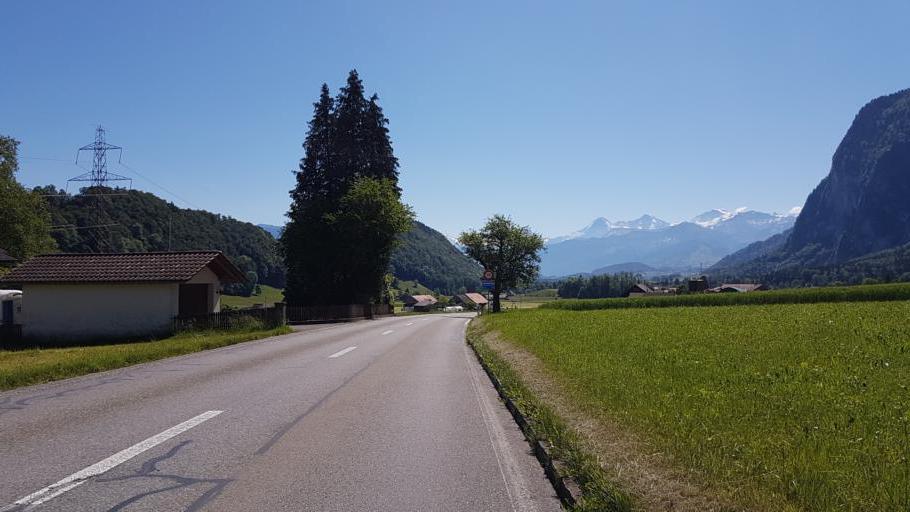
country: CH
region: Bern
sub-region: Thun District
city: Thierachern
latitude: 46.7139
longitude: 7.5668
